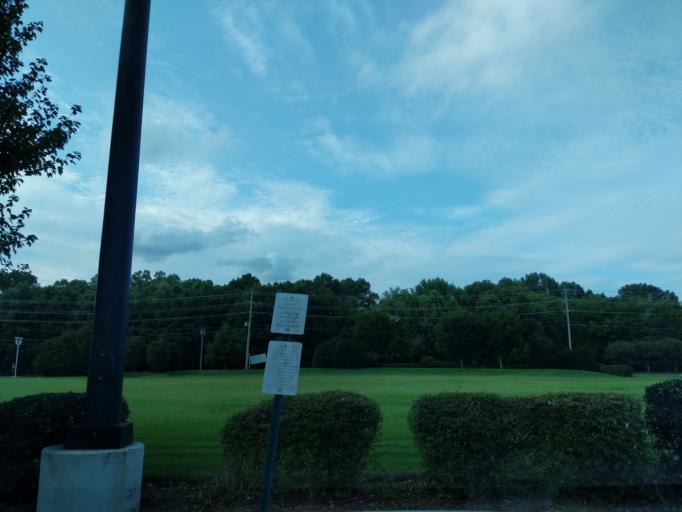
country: US
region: Tennessee
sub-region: Shelby County
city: Germantown
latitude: 35.0466
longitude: -89.7572
